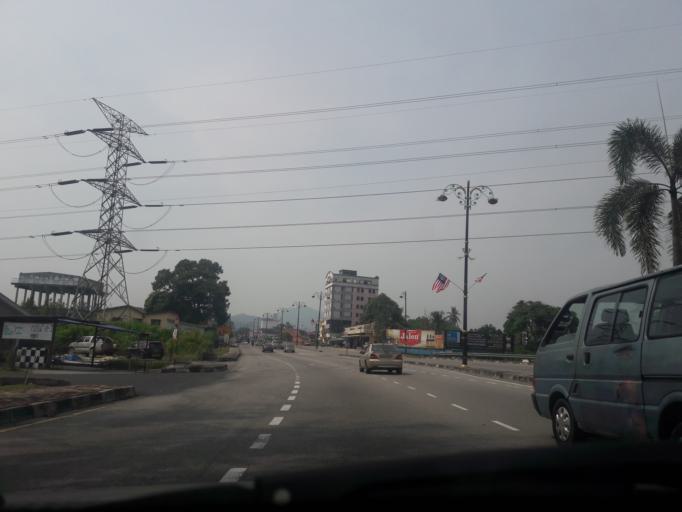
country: MY
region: Kedah
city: Kulim
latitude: 5.3791
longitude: 100.5528
